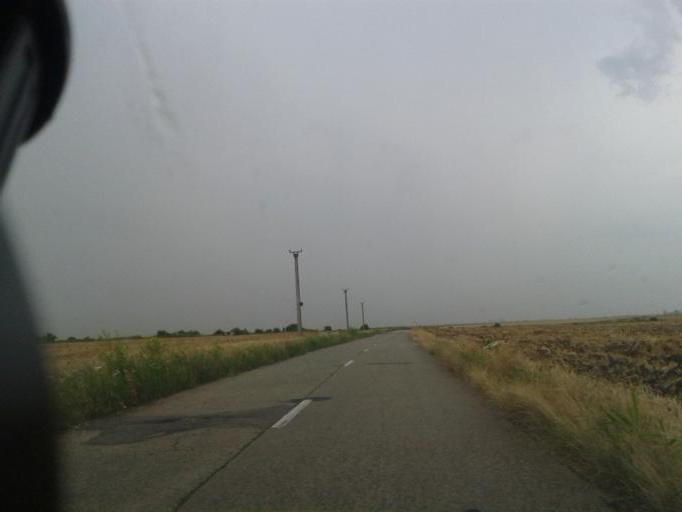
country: RO
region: Ialomita
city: Sinesti
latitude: 44.5402
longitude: 26.3932
